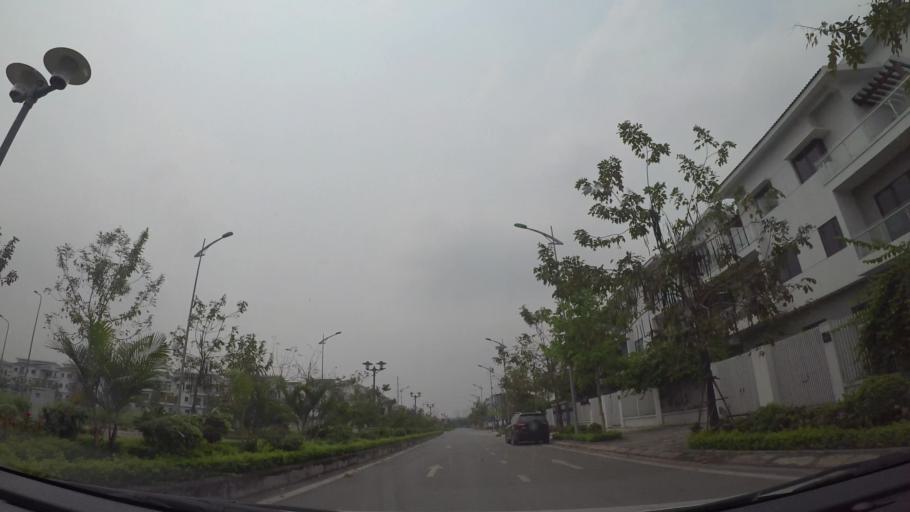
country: VN
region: Ha Noi
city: Cau Dien
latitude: 21.0285
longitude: 105.7480
